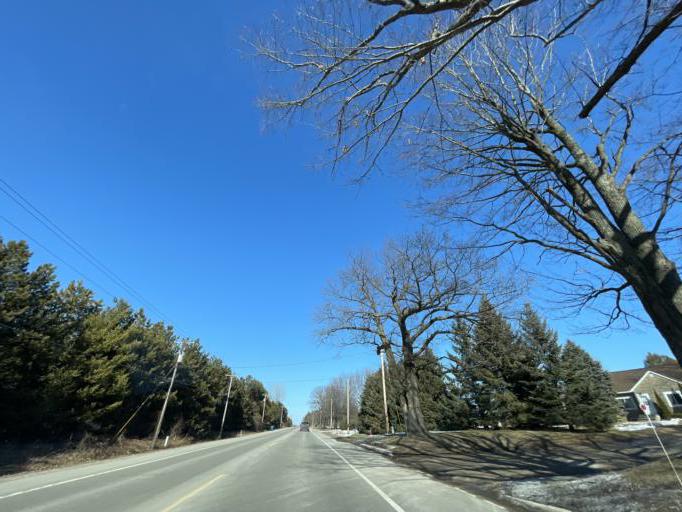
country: US
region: Wisconsin
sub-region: Brown County
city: Suamico
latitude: 44.6101
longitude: -88.0727
